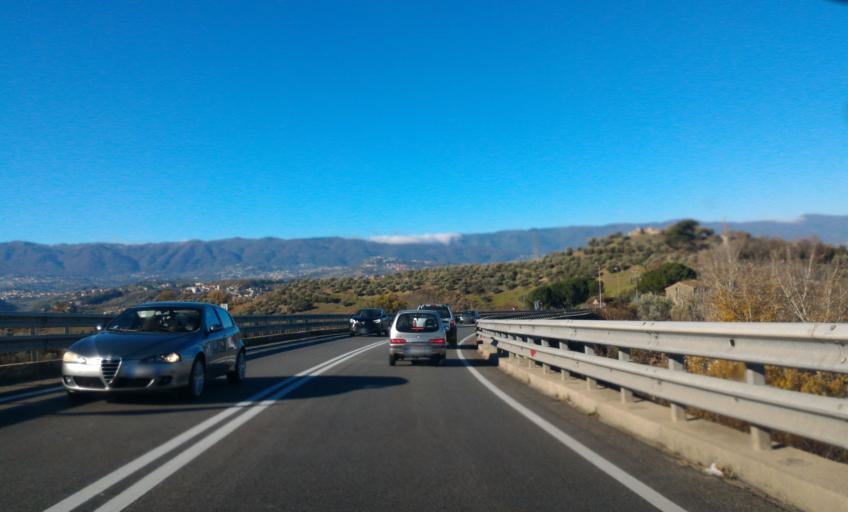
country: IT
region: Calabria
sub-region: Provincia di Cosenza
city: Cosenza
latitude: 39.2947
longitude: 16.2725
